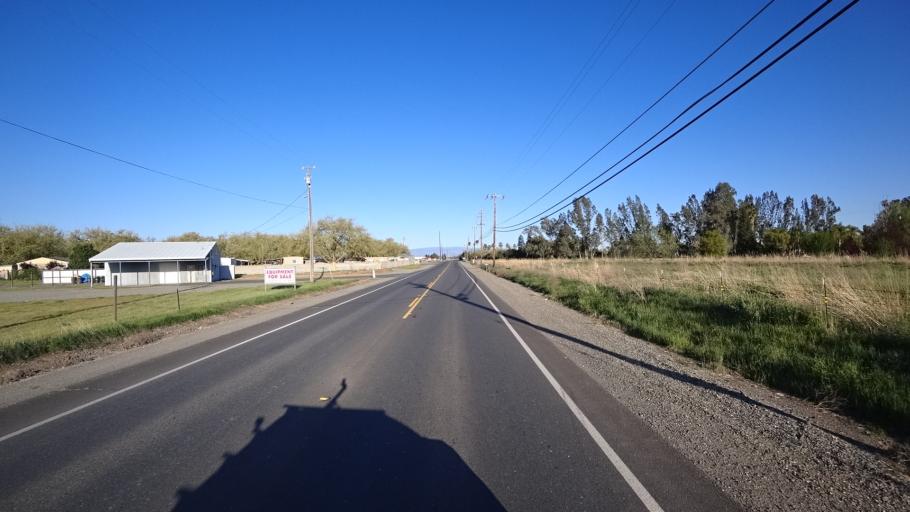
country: US
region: California
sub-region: Glenn County
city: Orland
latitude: 39.7538
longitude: -122.2133
